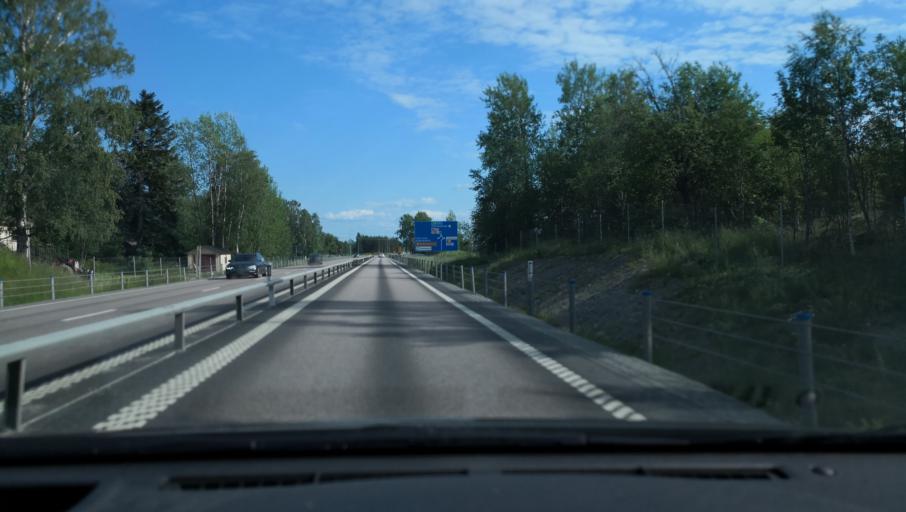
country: SE
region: Uppsala
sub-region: Enkopings Kommun
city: Enkoping
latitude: 59.6620
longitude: 17.0749
